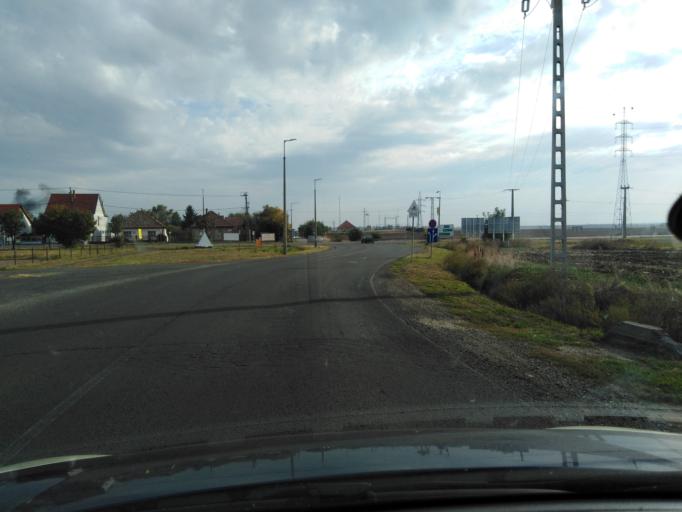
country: HU
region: Heves
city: Hatvan
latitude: 47.6626
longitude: 19.6434
